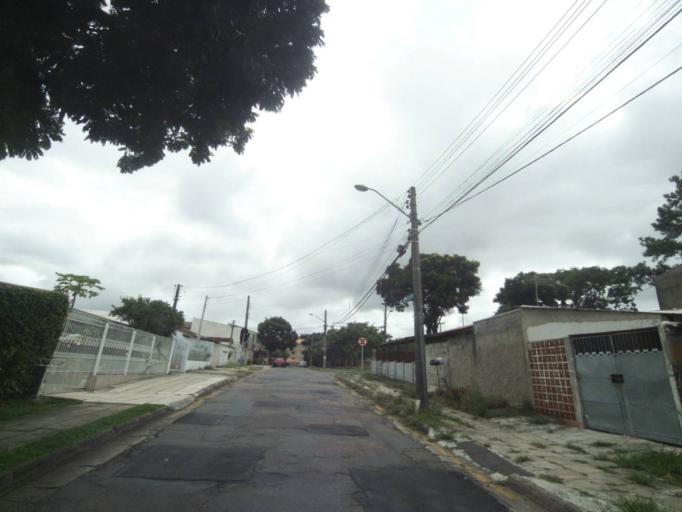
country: BR
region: Parana
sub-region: Curitiba
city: Curitiba
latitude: -25.4936
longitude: -49.2861
